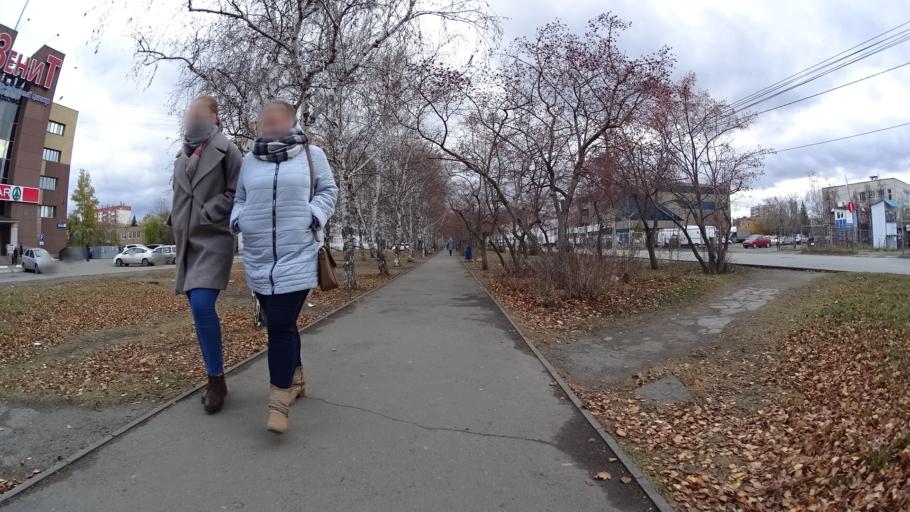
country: RU
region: Chelyabinsk
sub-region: Gorod Chelyabinsk
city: Chelyabinsk
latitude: 55.1920
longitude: 61.3217
